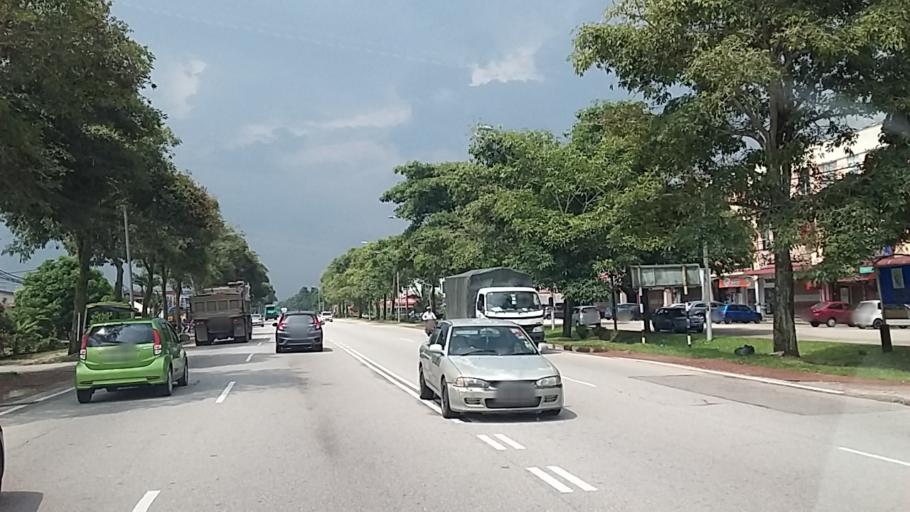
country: MY
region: Johor
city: Parit Raja
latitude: 1.8669
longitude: 103.1171
